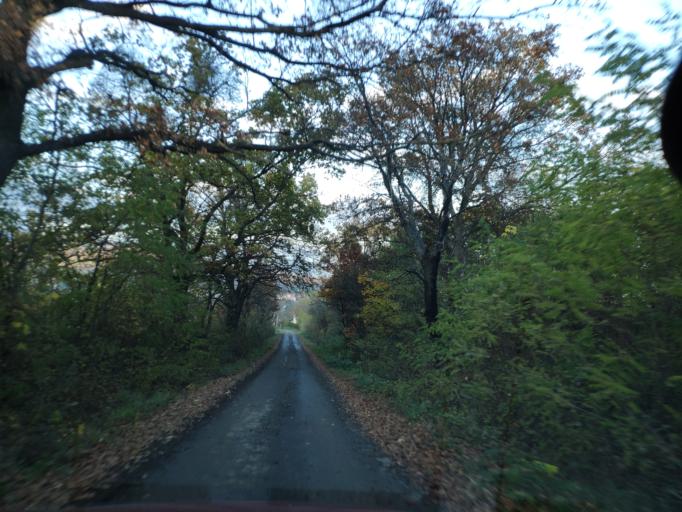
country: SK
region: Kosicky
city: Secovce
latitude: 48.6099
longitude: 21.5209
